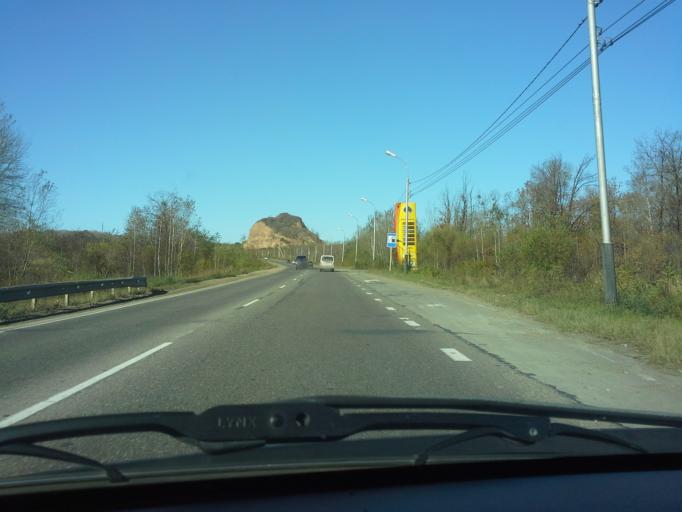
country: RU
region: Khabarovsk Krai
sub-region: Khabarovskiy Rayon
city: Khabarovsk
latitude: 48.5489
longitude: 135.0895
